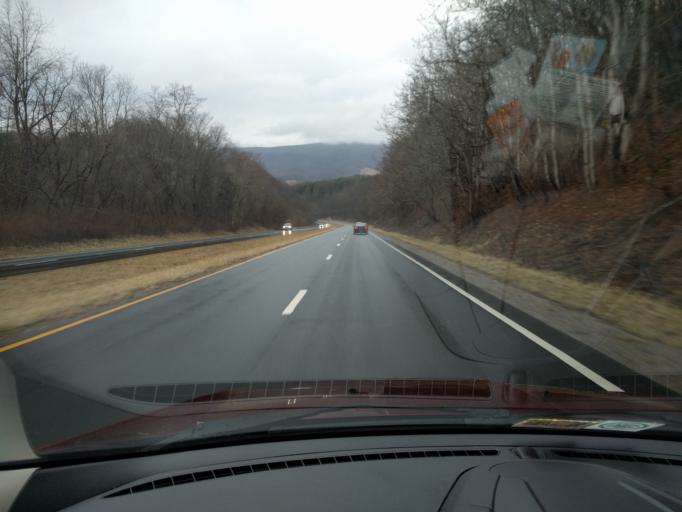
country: US
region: Virginia
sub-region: Montgomery County
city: Prices Fork
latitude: 37.3017
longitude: -80.5056
